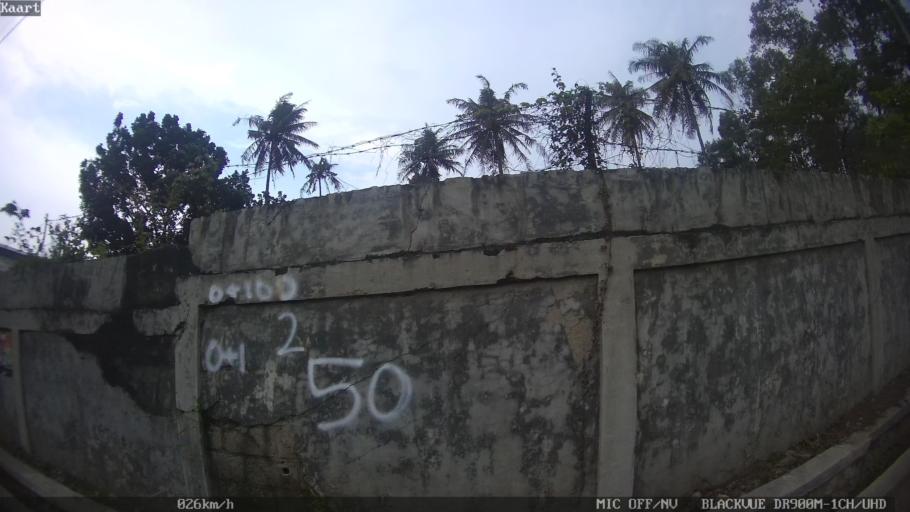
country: ID
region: Lampung
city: Bandarlampung
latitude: -5.4122
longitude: 105.2940
